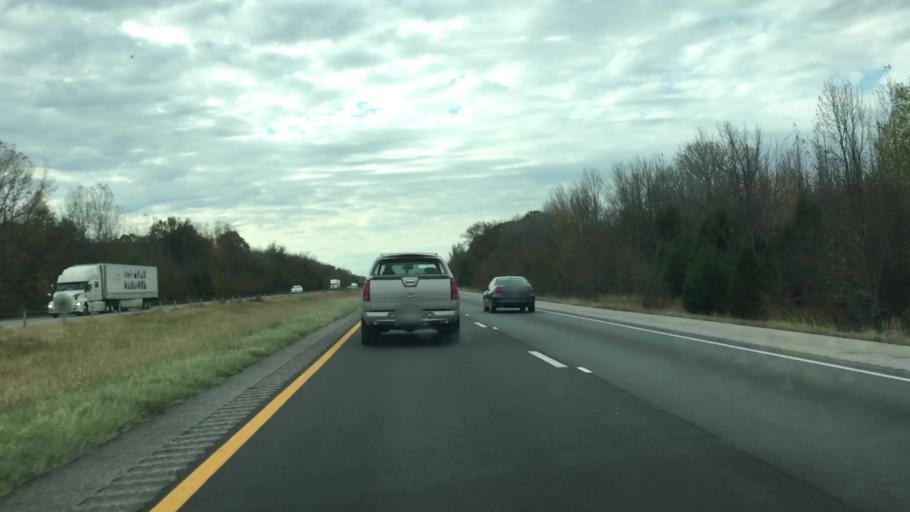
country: US
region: Arkansas
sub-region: Conway County
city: Morrilton
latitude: 35.1620
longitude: -92.6085
